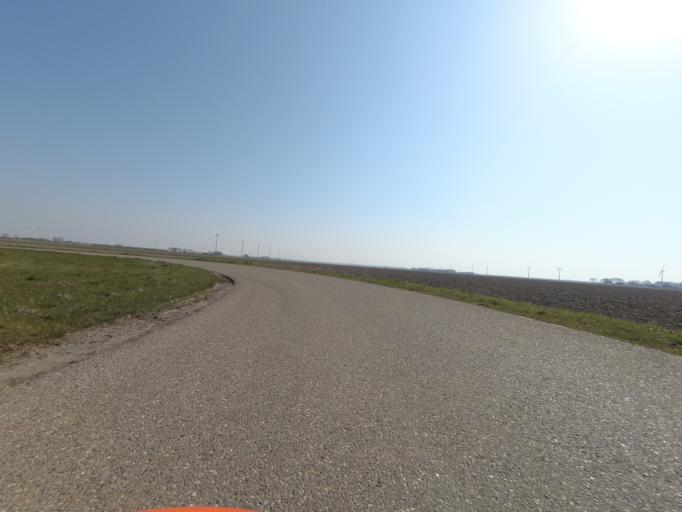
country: NL
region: Utrecht
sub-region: Gemeente Bunschoten
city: Spakenburg
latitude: 52.3063
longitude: 5.3409
